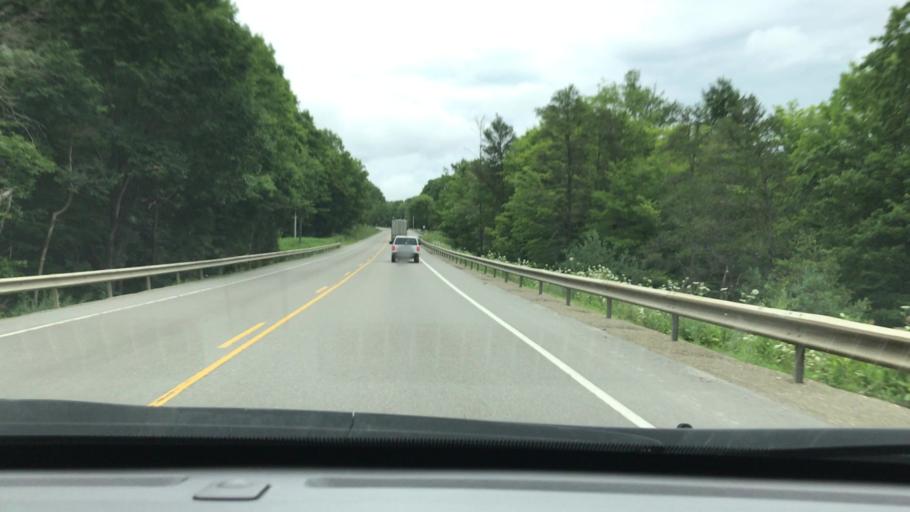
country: US
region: Pennsylvania
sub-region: McKean County
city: Kane
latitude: 41.6966
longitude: -78.6911
